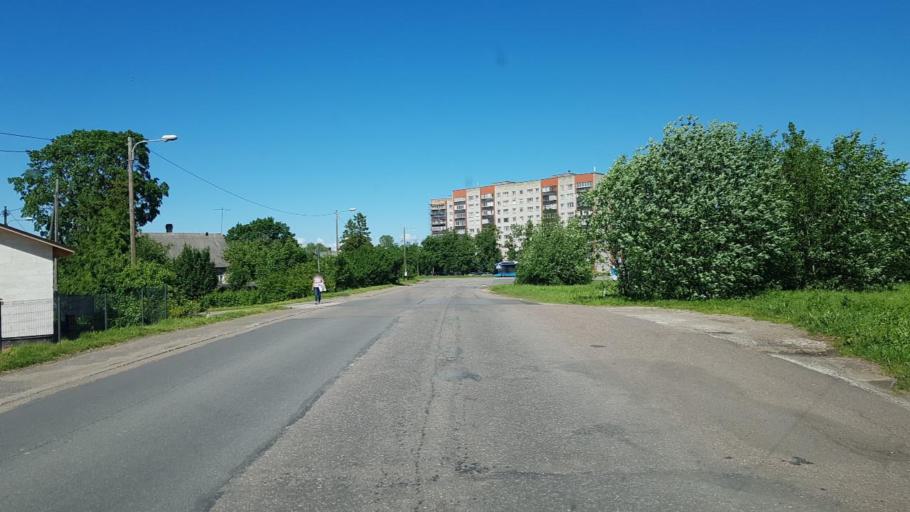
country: EE
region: Ida-Virumaa
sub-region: Narva linn
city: Narva
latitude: 59.3679
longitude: 28.1711
